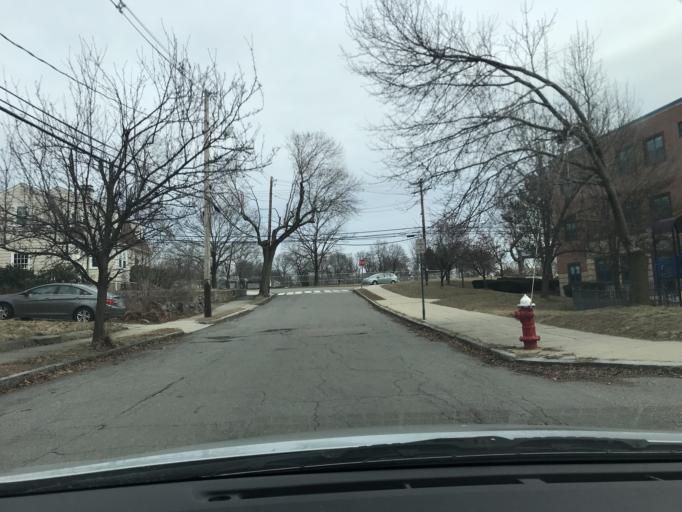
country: US
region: Massachusetts
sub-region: Middlesex County
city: Belmont
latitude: 42.4125
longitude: -71.1771
